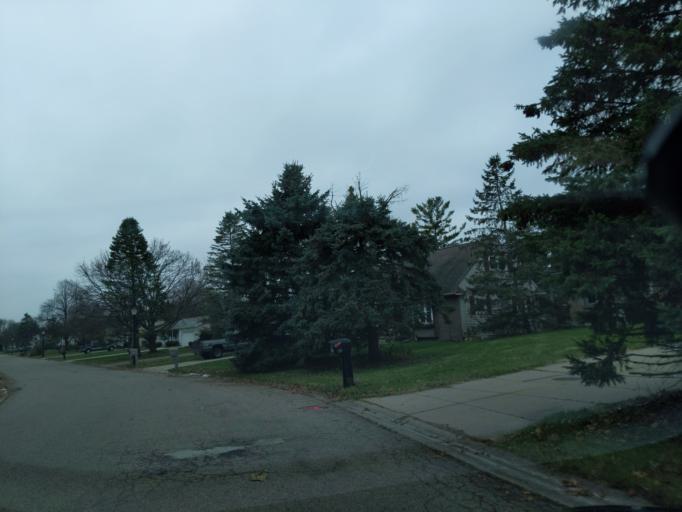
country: US
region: Michigan
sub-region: Eaton County
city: Waverly
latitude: 42.7324
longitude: -84.6317
